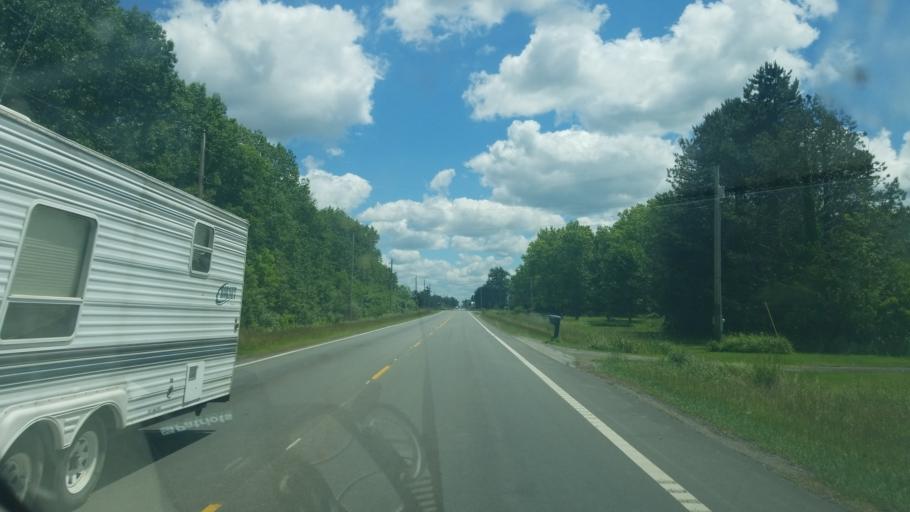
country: US
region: Ohio
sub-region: Huron County
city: New London
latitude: 41.0294
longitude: -82.3285
